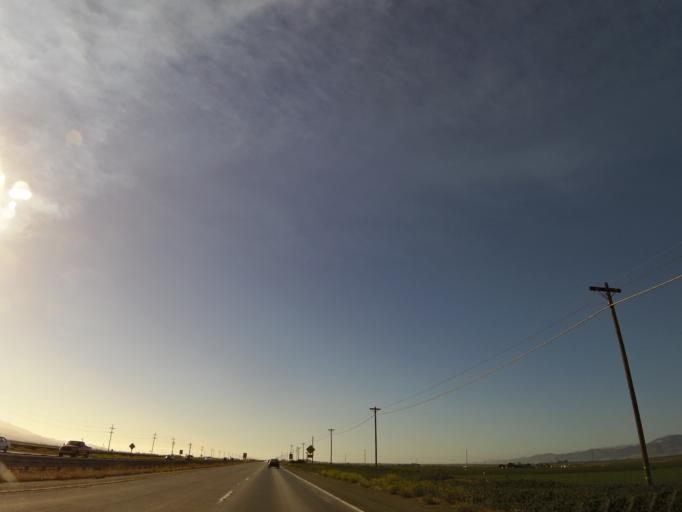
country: US
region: California
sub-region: Monterey County
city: Gonzales
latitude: 36.5346
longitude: -121.4789
